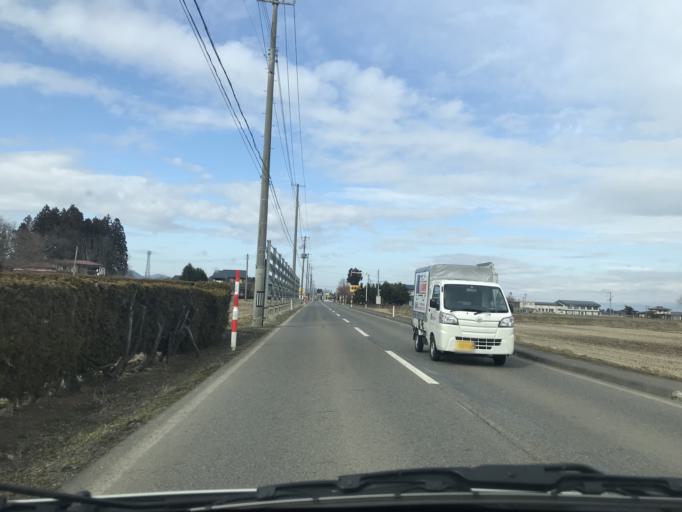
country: JP
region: Iwate
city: Hanamaki
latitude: 39.3542
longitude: 141.0493
